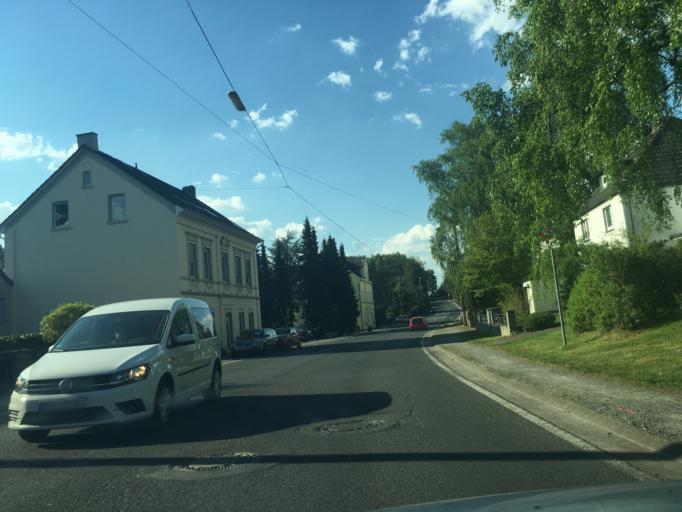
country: DE
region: North Rhine-Westphalia
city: Haan
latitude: 51.1785
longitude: 6.9874
